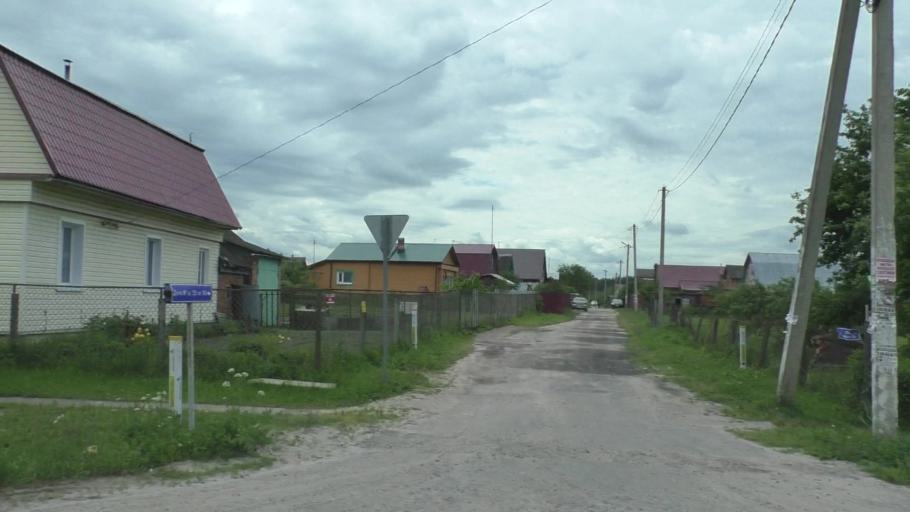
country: RU
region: Moskovskaya
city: Imeni Tsyurupy
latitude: 55.5041
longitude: 38.7799
